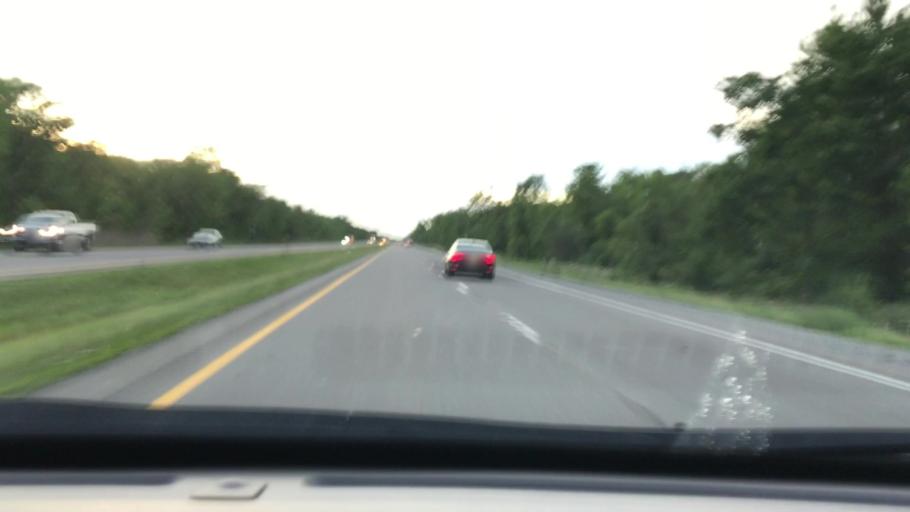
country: US
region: New York
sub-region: Niagara County
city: Niagara Falls
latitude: 43.0066
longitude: -79.0779
